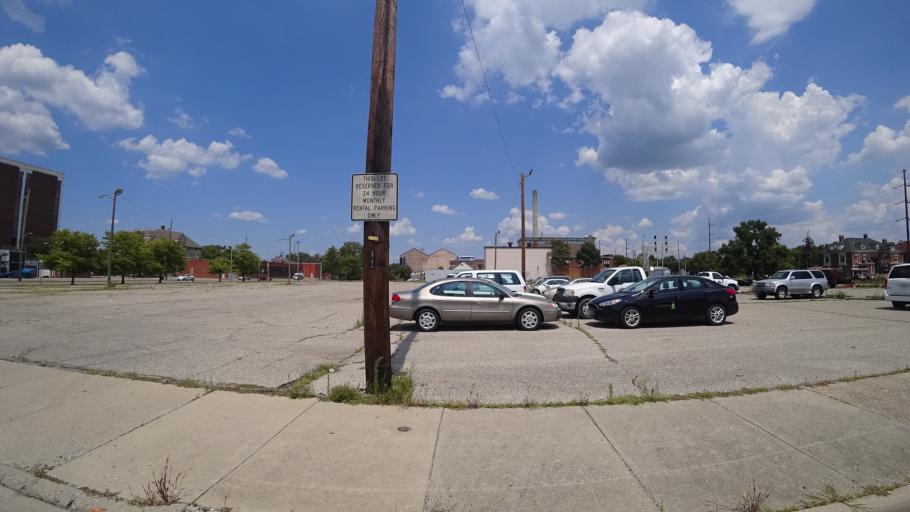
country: US
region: Ohio
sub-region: Butler County
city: Hamilton
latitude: 39.3999
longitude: -84.5574
